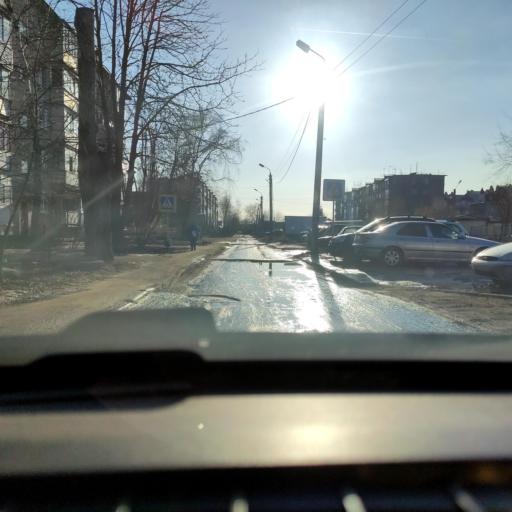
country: RU
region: Voronezj
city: Maslovka
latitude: 51.5358
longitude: 39.3421
